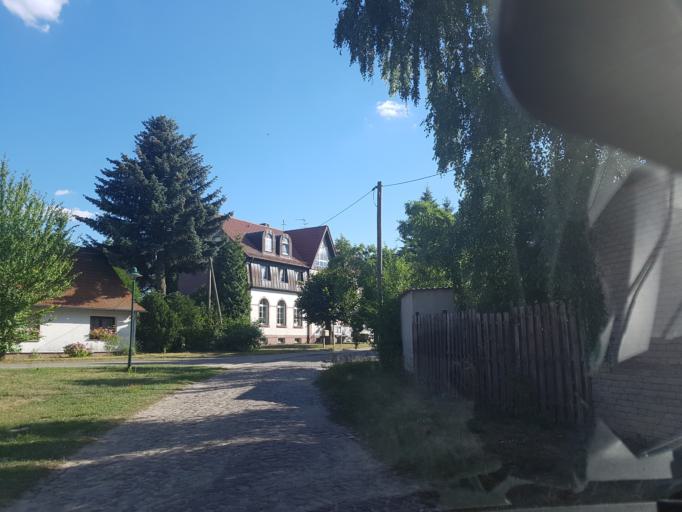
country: DE
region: Brandenburg
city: Juterbog
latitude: 51.9147
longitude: 13.1475
